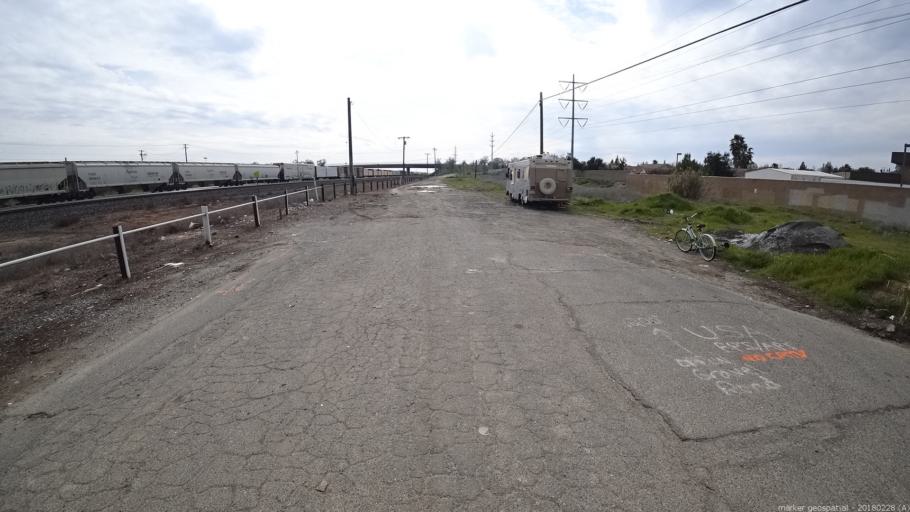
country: US
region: California
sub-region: Sacramento County
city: Antelope
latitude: 38.7057
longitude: -121.3331
